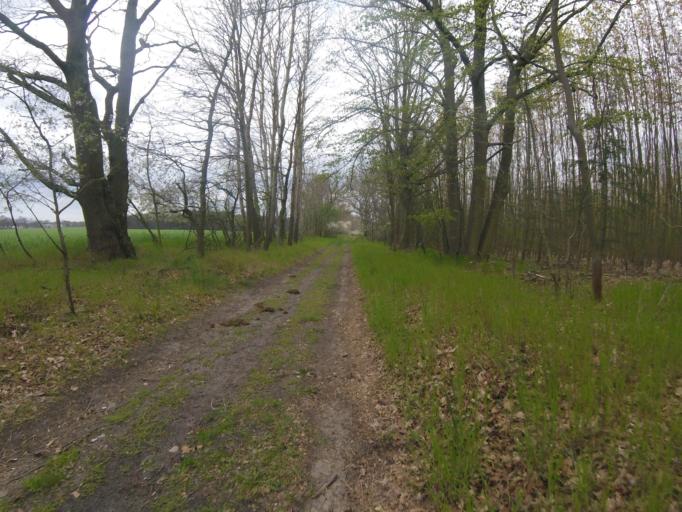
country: DE
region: Brandenburg
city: Mittenwalde
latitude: 52.2488
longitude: 13.5799
